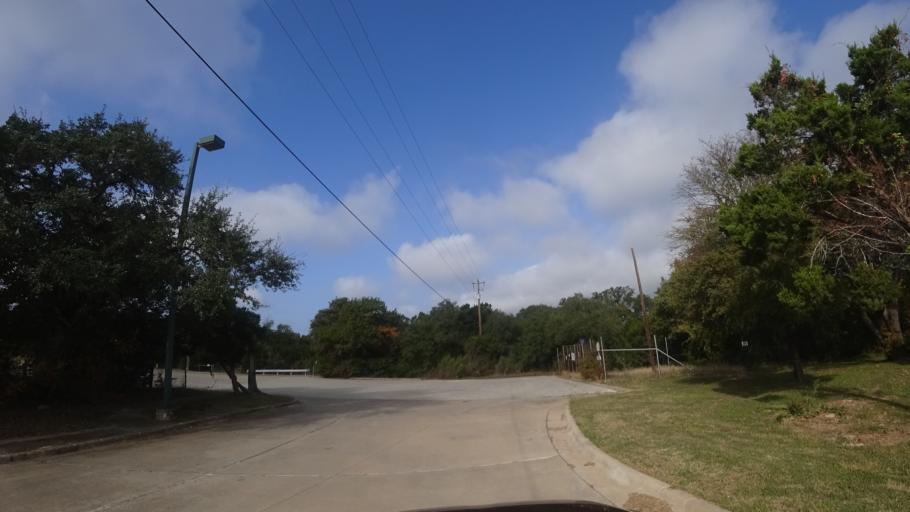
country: US
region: Texas
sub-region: Williamson County
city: Anderson Mill
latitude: 30.4044
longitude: -97.8372
